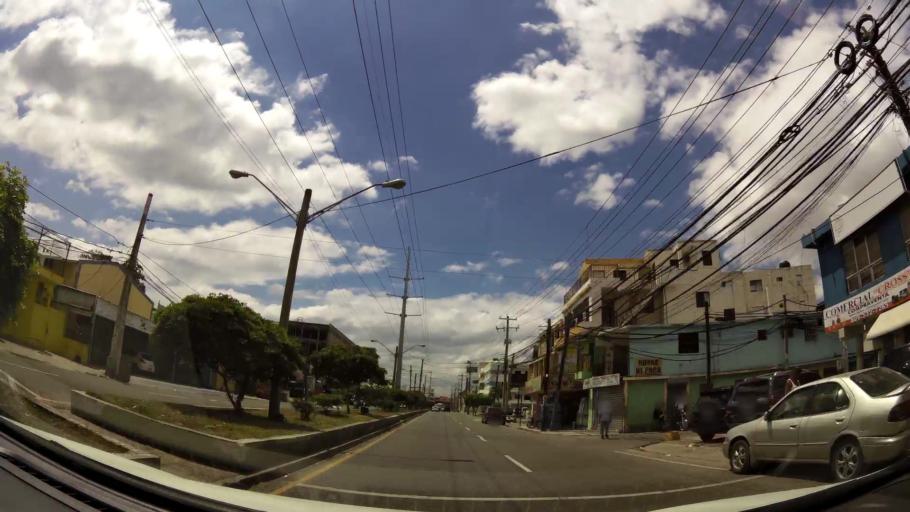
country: DO
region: Nacional
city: Bella Vista
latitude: 18.4349
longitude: -69.9596
